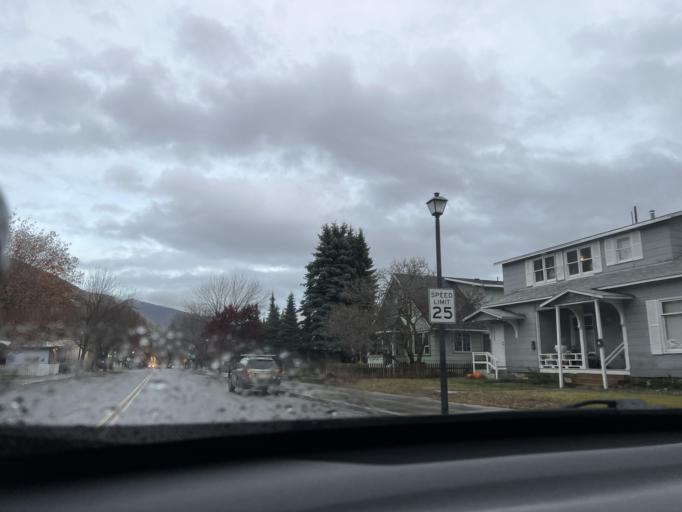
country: US
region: Washington
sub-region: Chelan County
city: Cashmere
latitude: 47.5218
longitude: -120.4673
